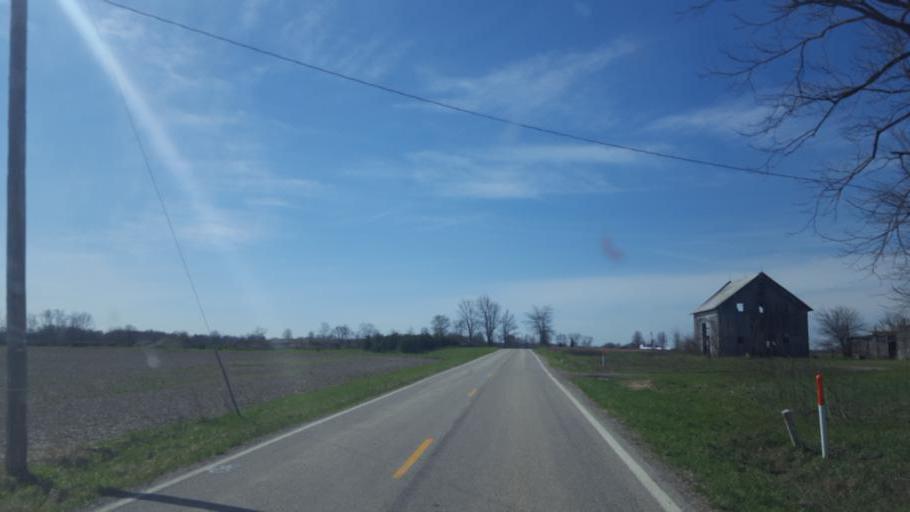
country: US
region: Ohio
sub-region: Delaware County
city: Ashley
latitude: 40.4692
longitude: -82.9631
